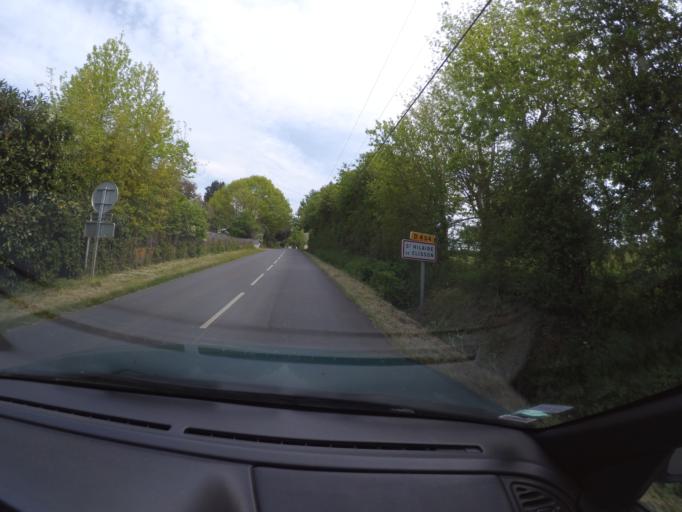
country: FR
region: Pays de la Loire
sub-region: Departement de la Loire-Atlantique
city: Saint-Hilaire-de-Clisson
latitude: 47.0619
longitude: -1.3150
